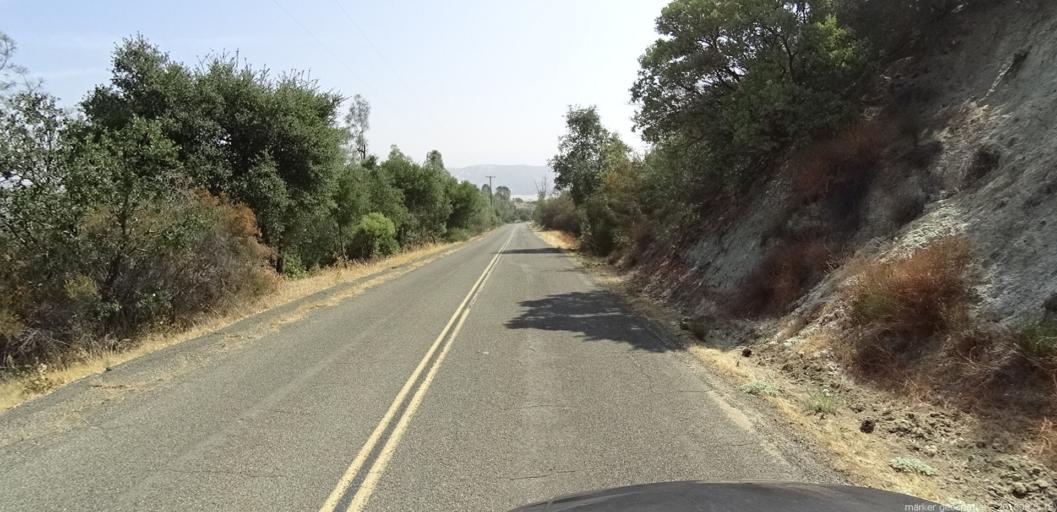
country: US
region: California
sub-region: San Luis Obispo County
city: San Miguel
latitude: 35.9208
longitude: -120.5277
